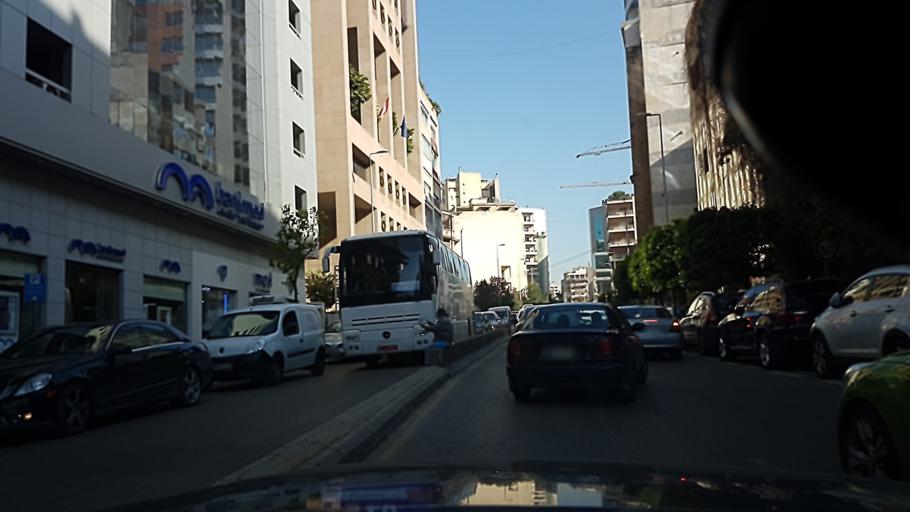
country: LB
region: Beyrouth
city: Beirut
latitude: 33.8923
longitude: 35.5119
